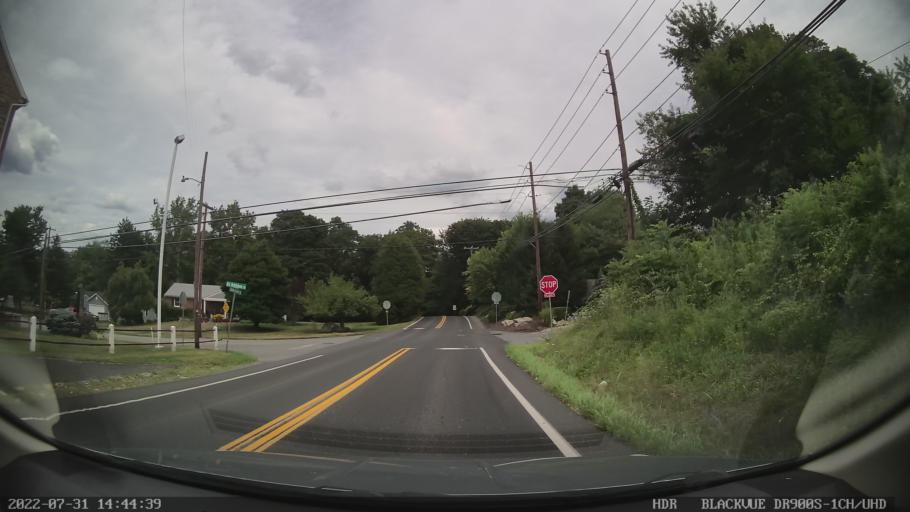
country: US
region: Pennsylvania
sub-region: Lehigh County
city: Fountain Hill
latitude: 40.5593
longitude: -75.3959
